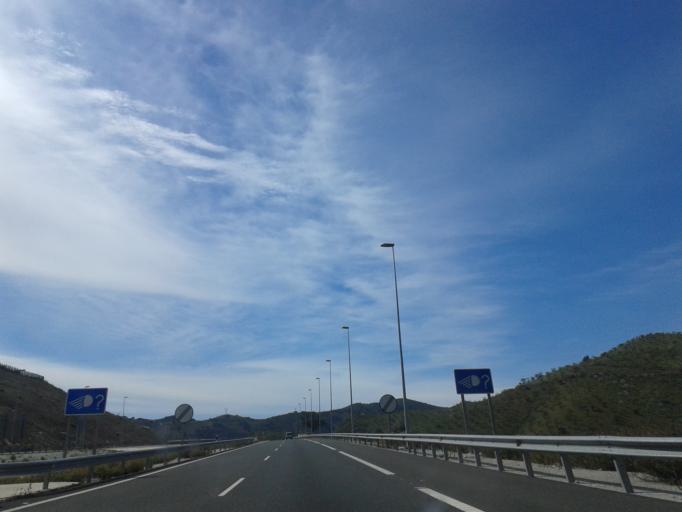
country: ES
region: Andalusia
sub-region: Provincia de Malaga
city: Casabermeja
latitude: 36.8929
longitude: -4.4668
